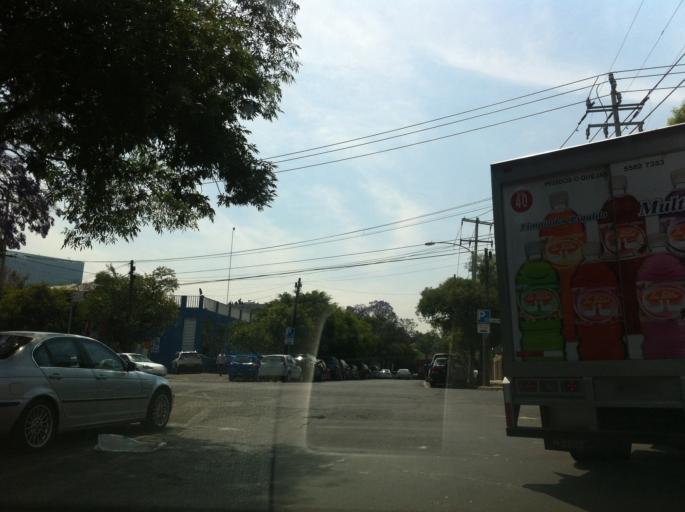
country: MX
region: Mexico City
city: Miguel Hidalgo
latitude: 19.4270
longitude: -99.2104
